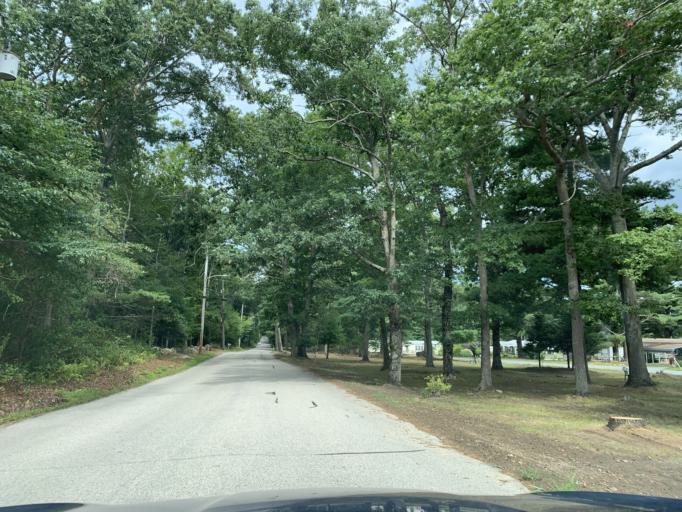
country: US
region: Rhode Island
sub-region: Washington County
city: Exeter
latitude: 41.5522
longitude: -71.6211
